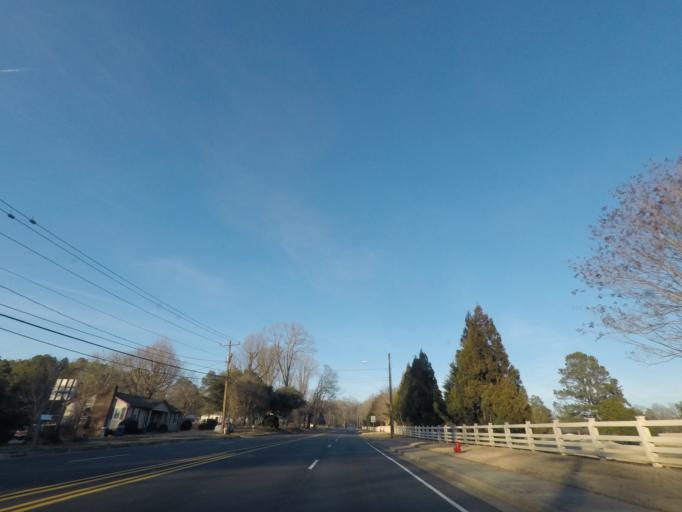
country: US
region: North Carolina
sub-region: Durham County
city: Durham
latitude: 36.0290
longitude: -78.9530
